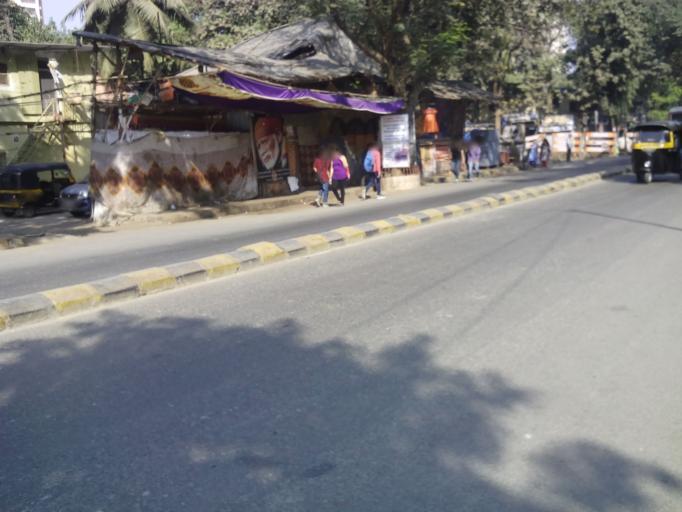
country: IN
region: Maharashtra
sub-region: Mumbai Suburban
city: Borivli
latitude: 19.2071
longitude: 72.8703
